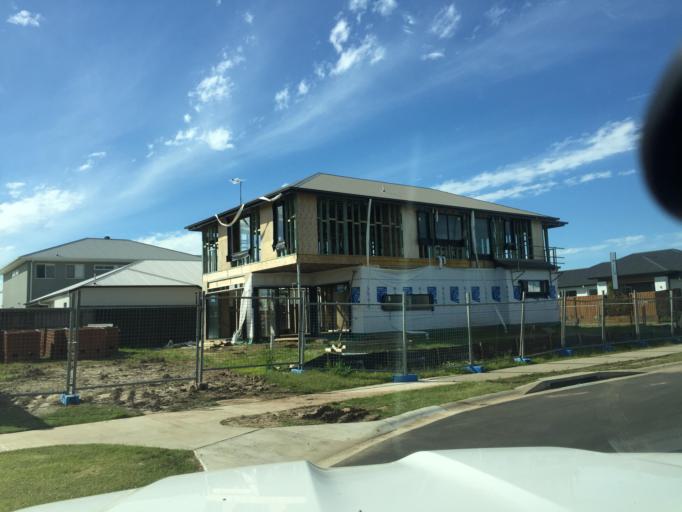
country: AU
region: Queensland
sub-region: Moreton Bay
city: Morayfield
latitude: -27.1236
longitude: 152.9963
